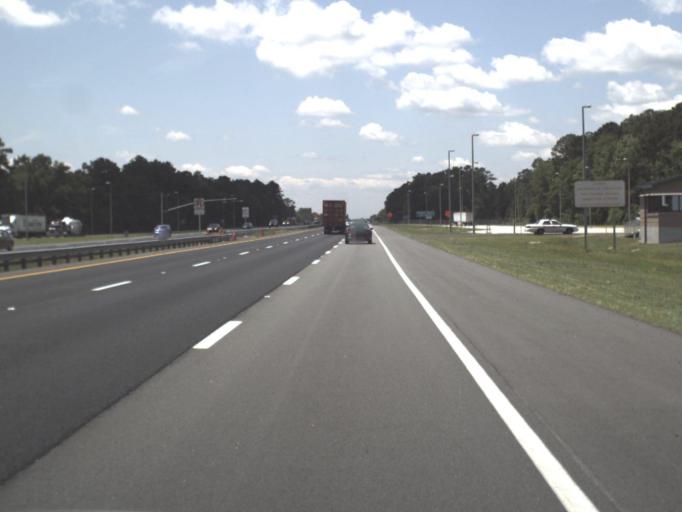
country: US
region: Georgia
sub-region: Camden County
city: Kingsland
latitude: 30.7273
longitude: -81.6633
